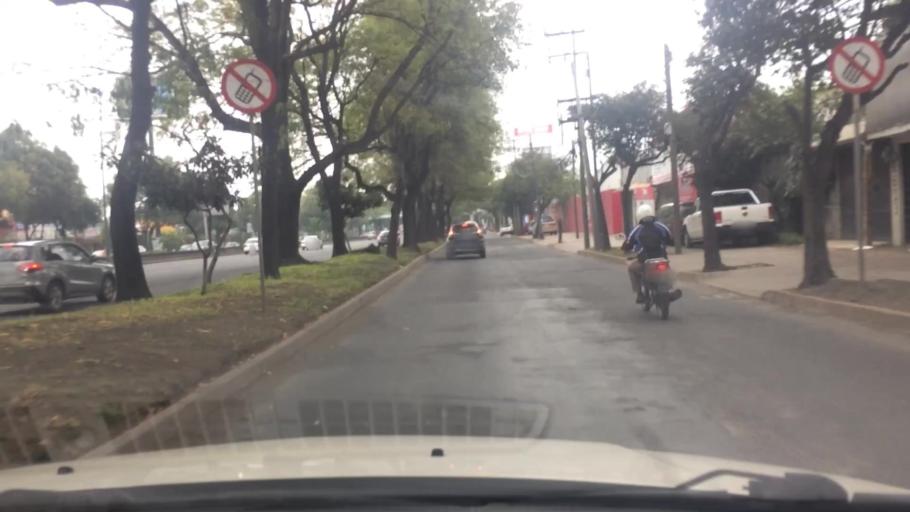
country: MX
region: Mexico City
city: Xochimilco
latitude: 19.2834
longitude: -99.1309
